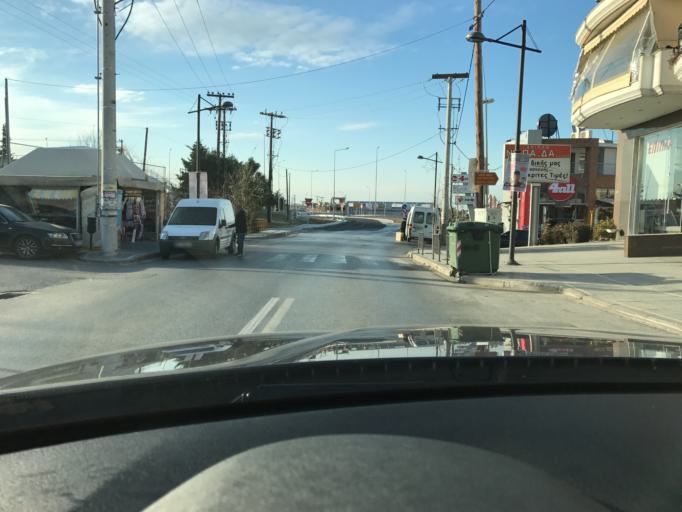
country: GR
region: Central Macedonia
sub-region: Nomos Thessalonikis
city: Efkarpia
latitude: 40.6814
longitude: 22.9478
